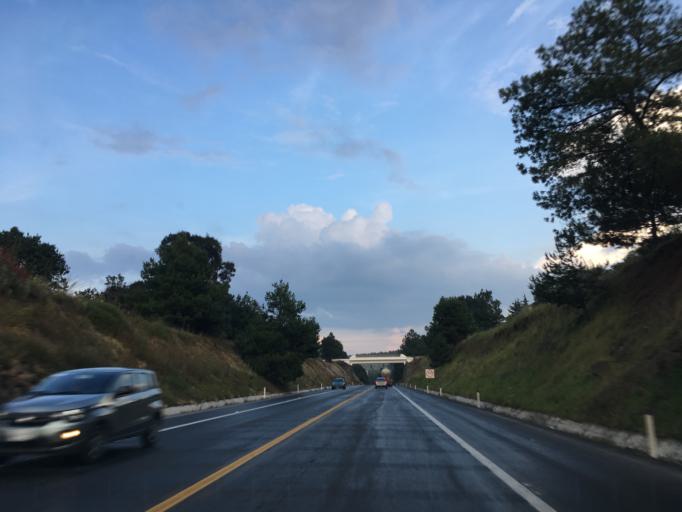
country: MX
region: Michoacan
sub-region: Patzcuaro
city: Santa Maria Huiramangaro (San Juan Tumbio)
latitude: 19.4896
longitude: -101.7129
